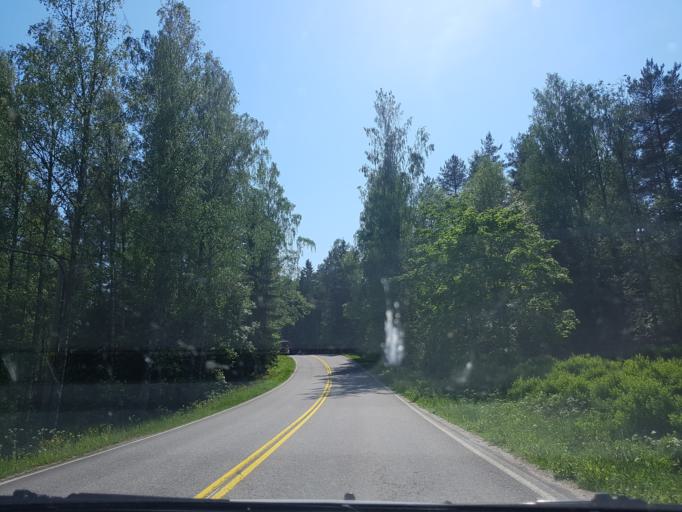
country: FI
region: Uusimaa
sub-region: Helsinki
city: Vihti
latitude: 60.3071
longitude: 24.3988
